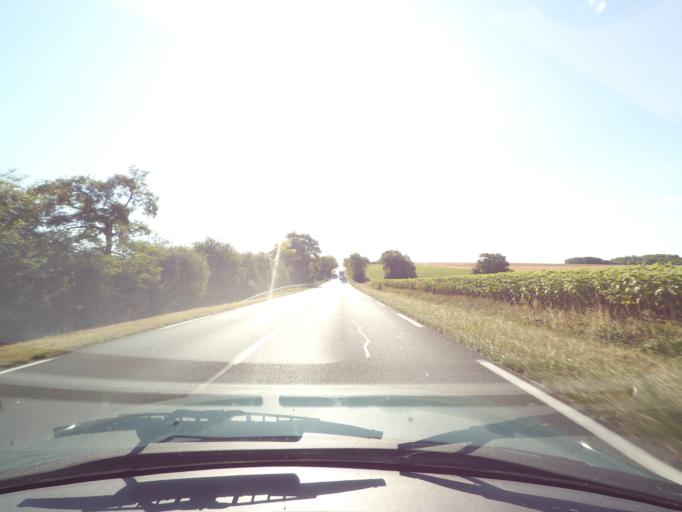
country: FR
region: Poitou-Charentes
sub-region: Departement de la Vienne
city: Ayron
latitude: 46.6541
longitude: 0.1151
